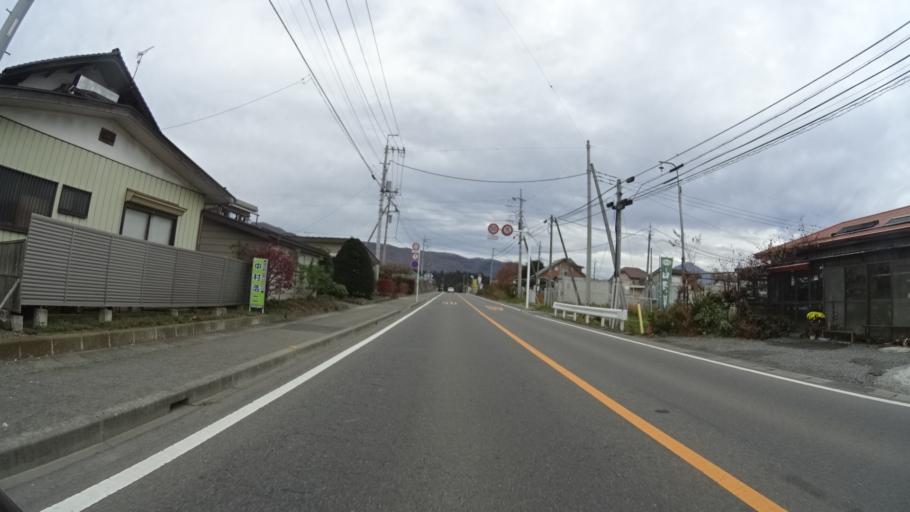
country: JP
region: Gunma
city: Numata
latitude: 36.6632
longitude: 139.1453
